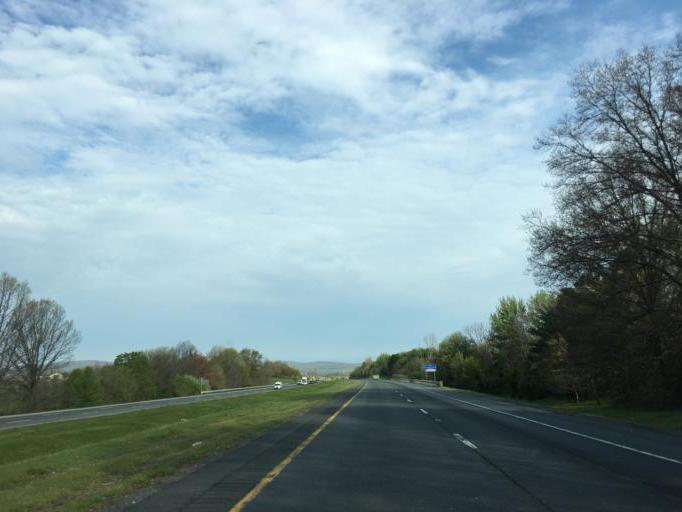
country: US
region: Maryland
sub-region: Frederick County
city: Middletown
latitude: 39.4597
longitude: -77.5108
